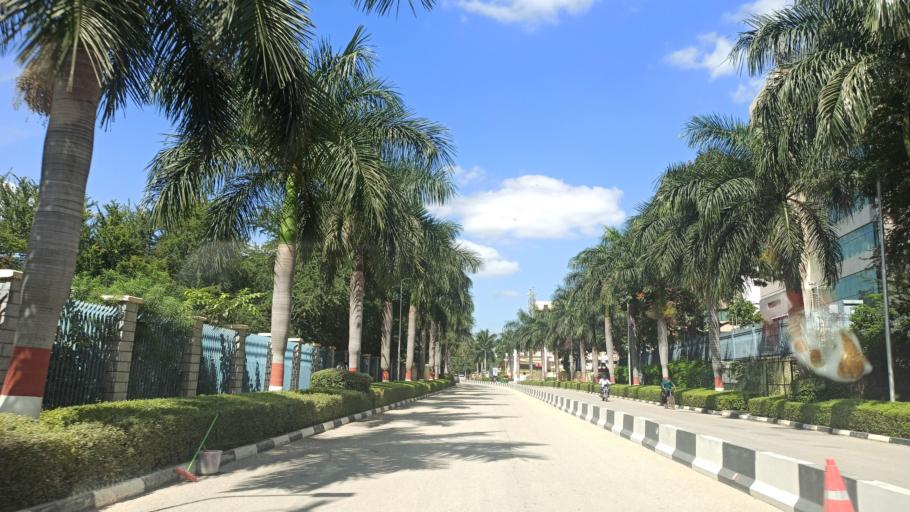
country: IN
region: Karnataka
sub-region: Bangalore Urban
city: Bangalore
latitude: 12.9243
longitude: 77.6859
